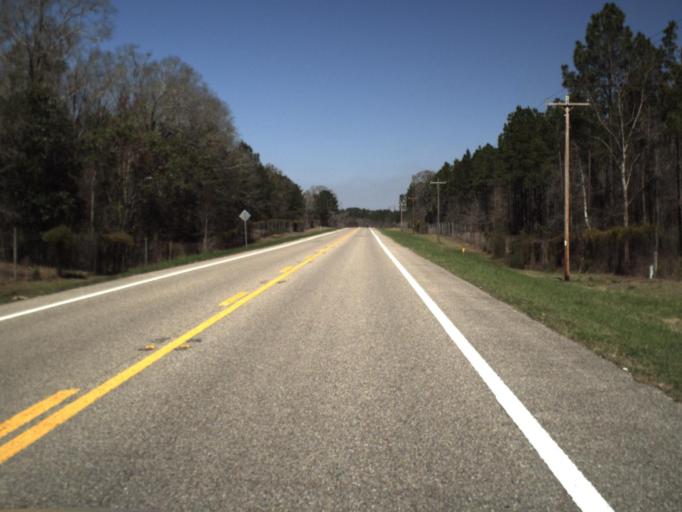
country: US
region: Florida
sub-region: Calhoun County
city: Blountstown
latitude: 30.5926
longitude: -85.0262
